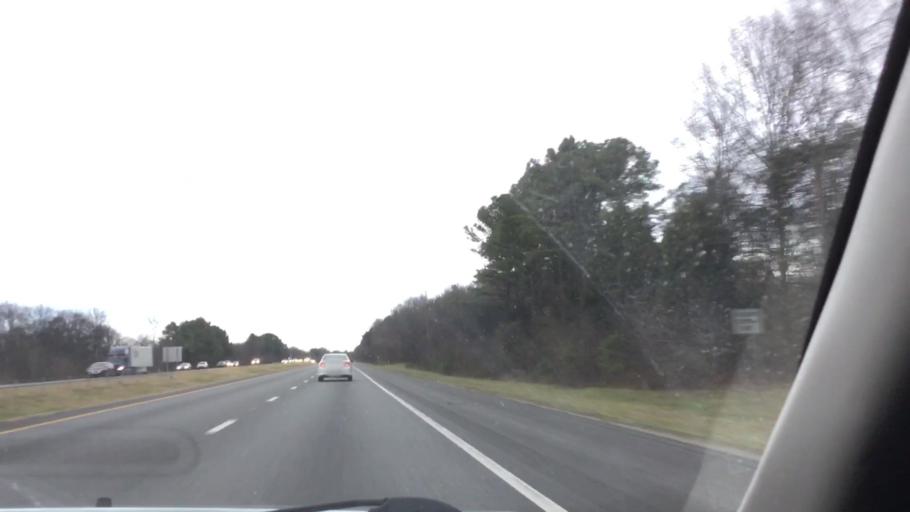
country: US
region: Tennessee
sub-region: Williamson County
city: Thompson's Station
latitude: 35.7669
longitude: -86.8646
